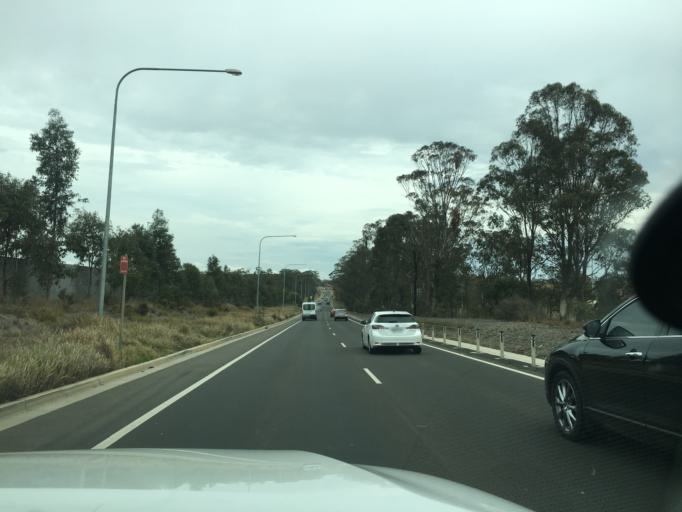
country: AU
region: New South Wales
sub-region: Campbelltown Municipality
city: Denham Court
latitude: -33.9780
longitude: 150.8070
